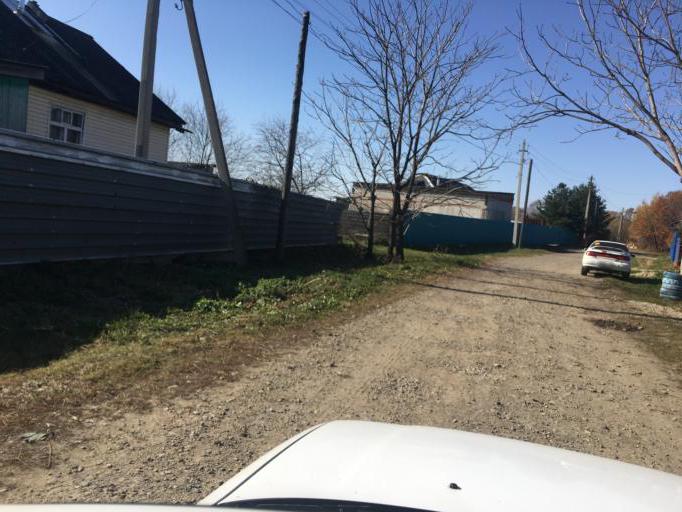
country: RU
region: Primorskiy
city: Dal'nerechensk
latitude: 45.9072
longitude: 133.7929
